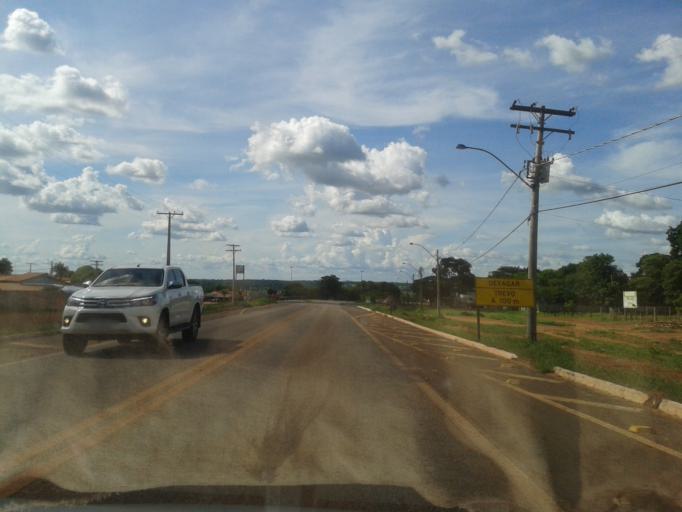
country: BR
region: Goias
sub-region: Mozarlandia
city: Mozarlandia
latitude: -15.0950
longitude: -50.6195
